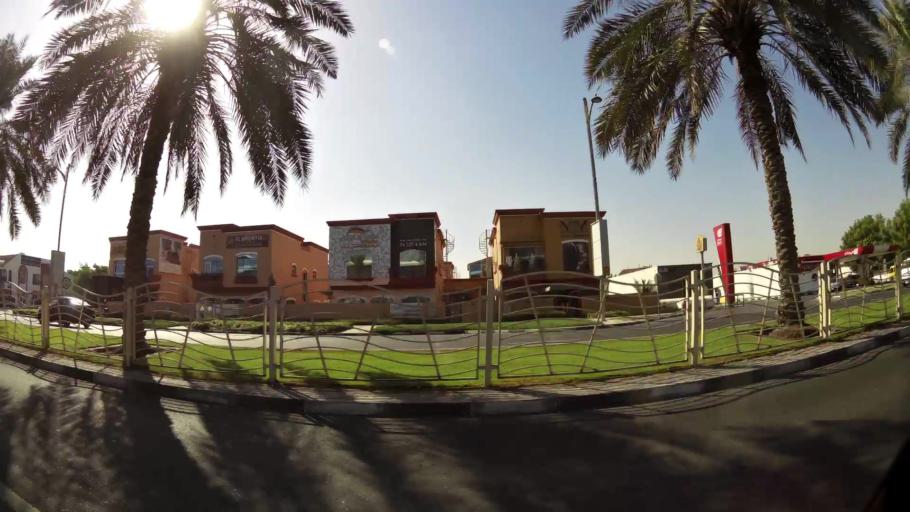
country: AE
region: Dubai
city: Dubai
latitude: 25.1838
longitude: 55.2268
